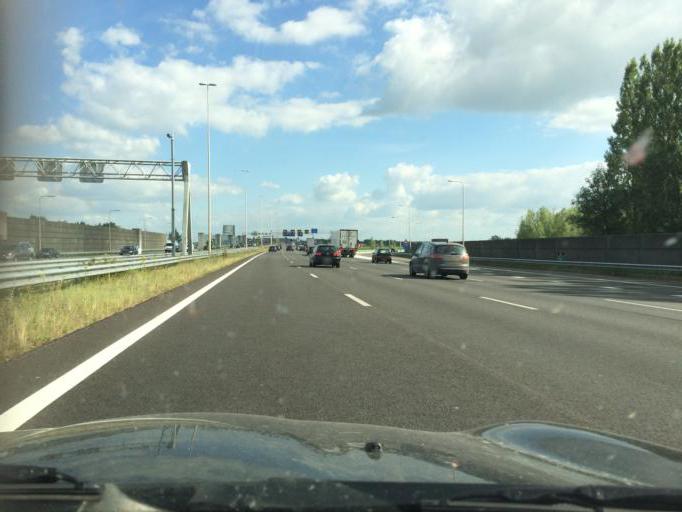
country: NL
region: Utrecht
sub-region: Gemeente Vianen
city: Vianen
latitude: 52.0063
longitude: 5.0737
